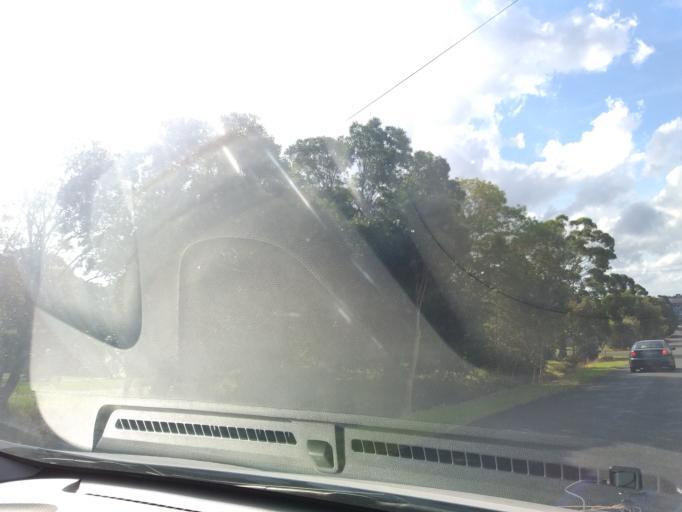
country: AU
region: New South Wales
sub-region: Wollongong
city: Helensburgh
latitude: -34.1978
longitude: 150.9807
